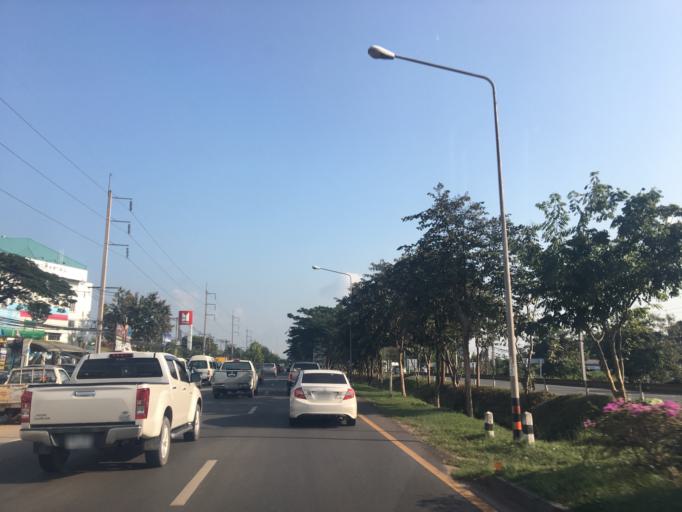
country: TH
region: Phayao
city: Phayao
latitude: 19.1696
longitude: 99.9079
